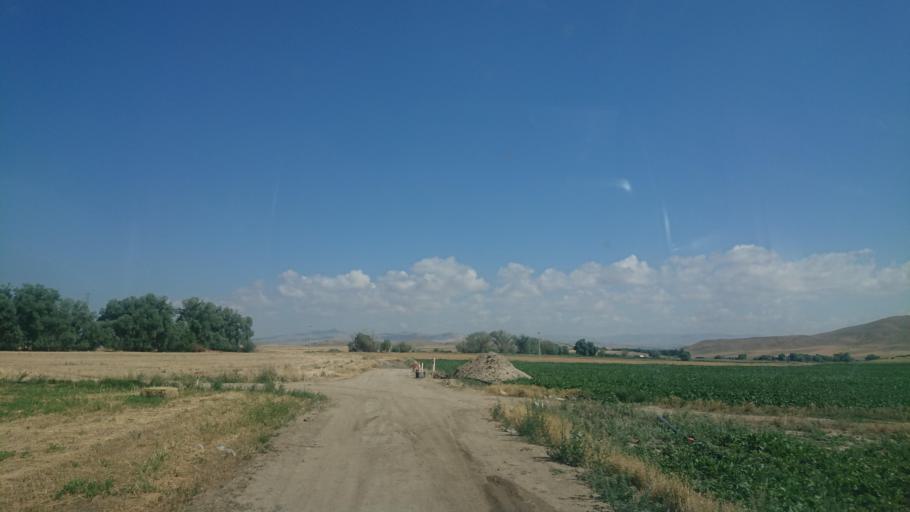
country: TR
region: Aksaray
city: Sariyahsi
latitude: 38.9958
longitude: 33.8950
